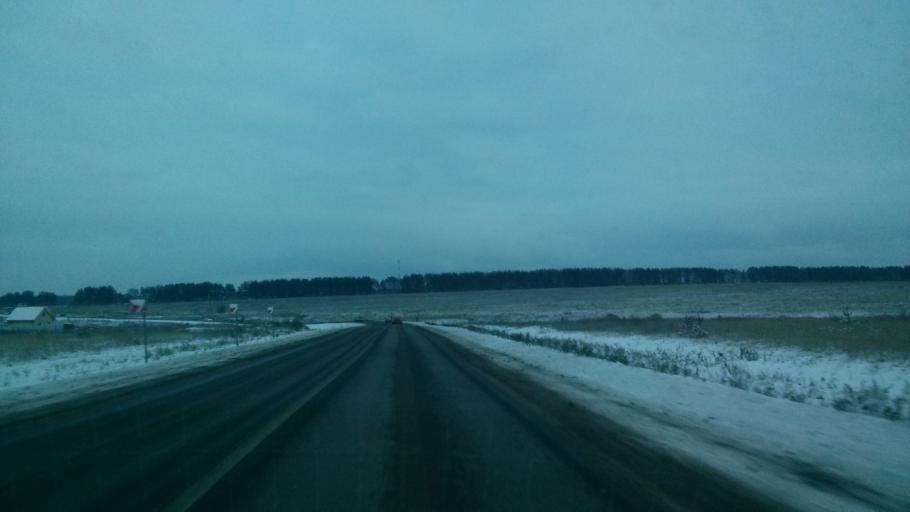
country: RU
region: Nizjnij Novgorod
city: Bogorodsk
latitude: 56.0864
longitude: 43.5001
